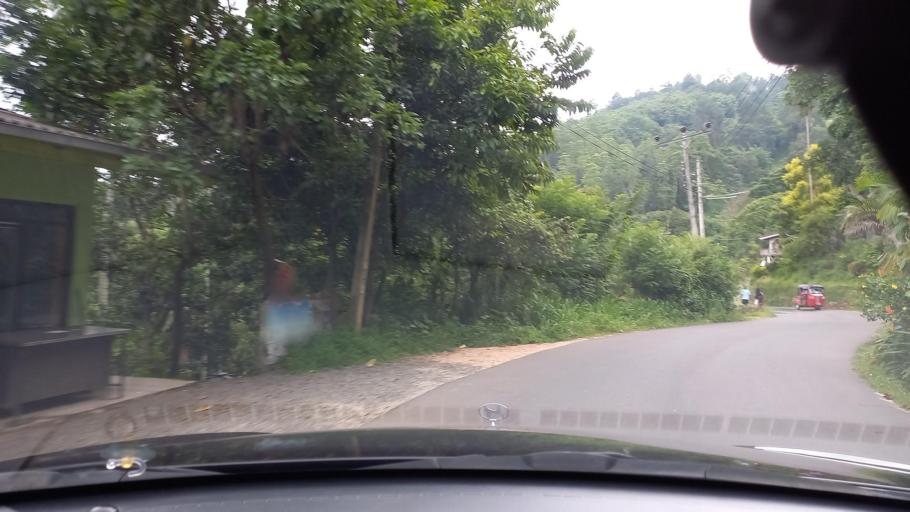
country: LK
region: Central
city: Gampola
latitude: 7.2080
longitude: 80.6259
